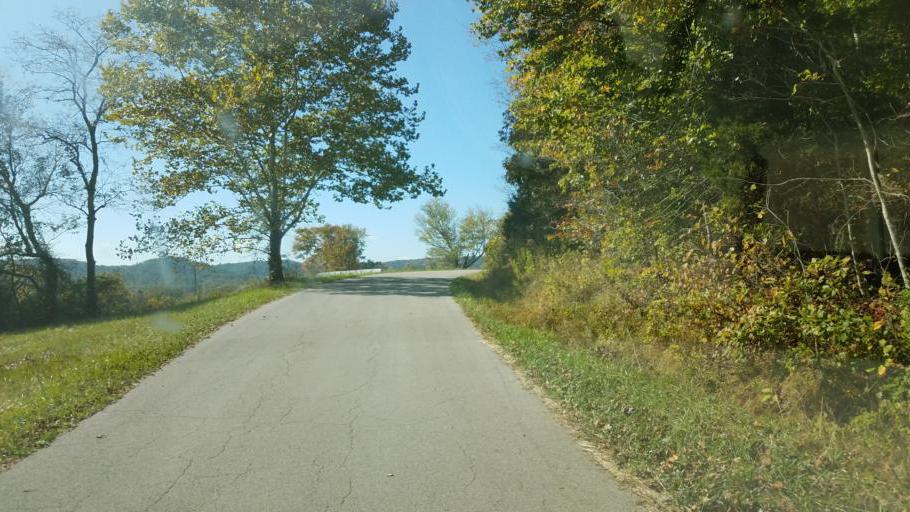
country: US
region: Kentucky
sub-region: Fleming County
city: Flemingsburg
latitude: 38.4443
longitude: -83.5662
